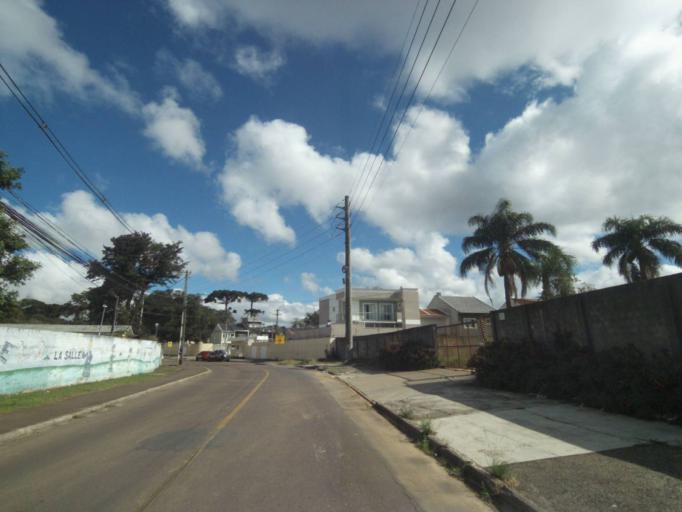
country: BR
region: Parana
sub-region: Sao Jose Dos Pinhais
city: Sao Jose dos Pinhais
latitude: -25.5314
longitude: -49.2914
